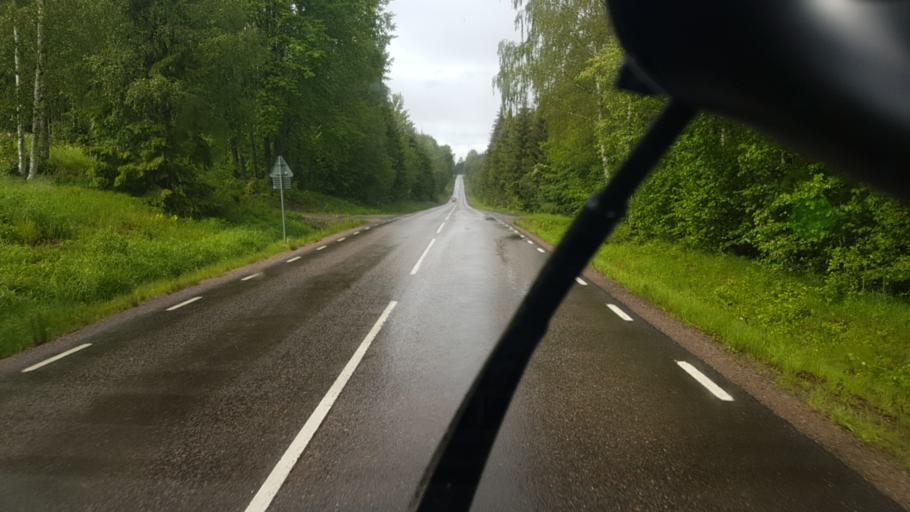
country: SE
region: Vaermland
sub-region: Eda Kommun
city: Amotfors
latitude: 59.7221
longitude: 12.4269
